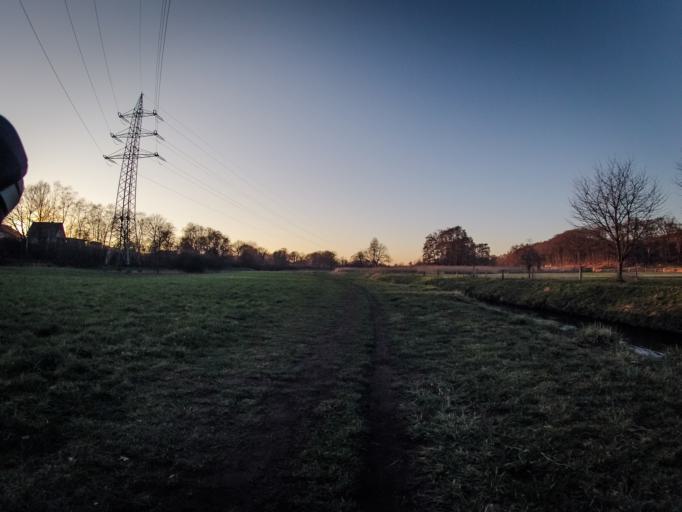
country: DE
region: Lower Saxony
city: Wallenhorst
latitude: 52.3108
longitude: 7.9807
